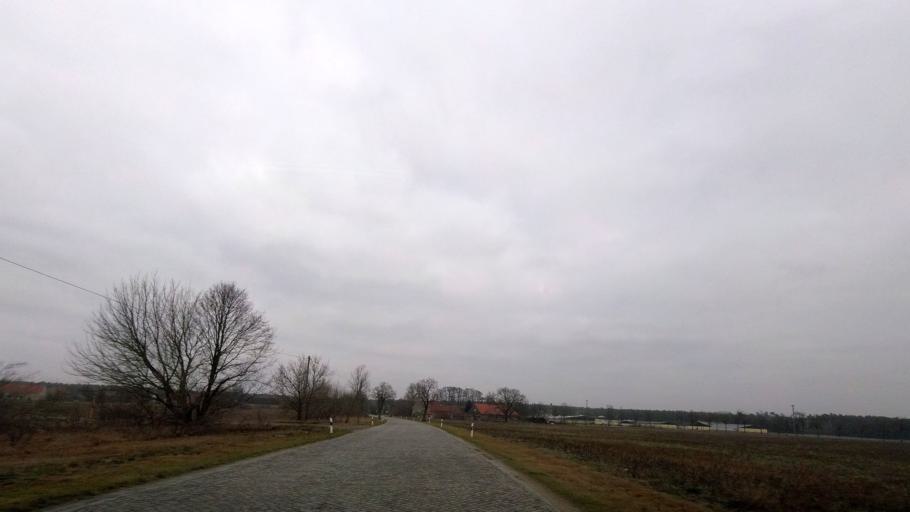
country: DE
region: Brandenburg
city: Beelitz
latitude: 52.1351
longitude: 12.9889
